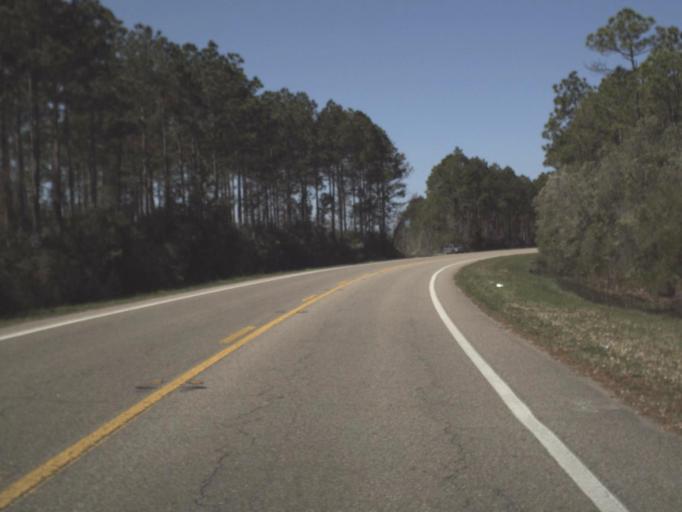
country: US
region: Florida
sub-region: Gulf County
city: Port Saint Joe
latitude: 29.7766
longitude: -85.2943
